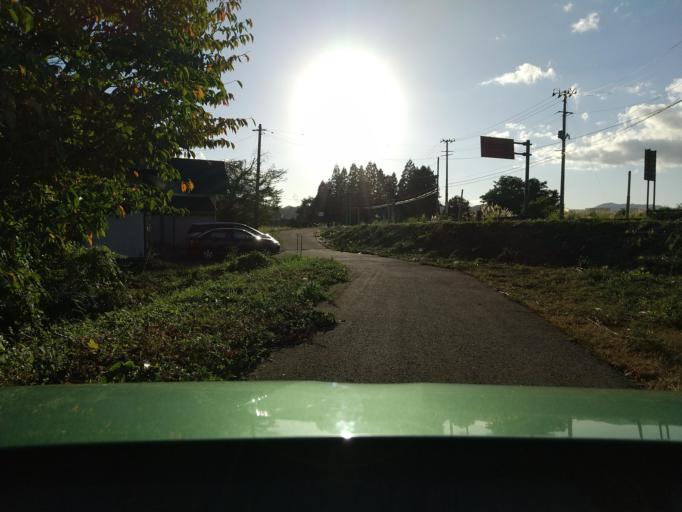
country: JP
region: Akita
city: Kakunodatemachi
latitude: 39.6135
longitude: 140.5804
